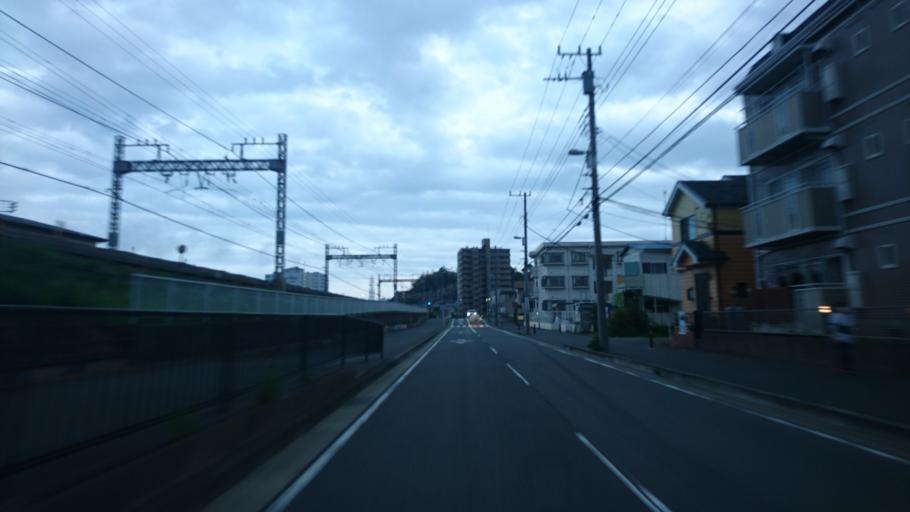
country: JP
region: Kanagawa
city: Fujisawa
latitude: 35.3536
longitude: 139.4739
